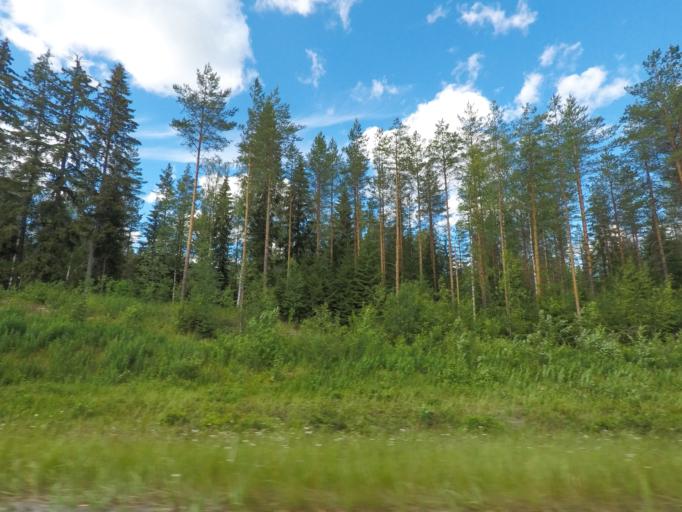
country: FI
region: Central Finland
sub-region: Jyvaeskylae
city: Hankasalmi
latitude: 62.2927
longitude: 26.4198
